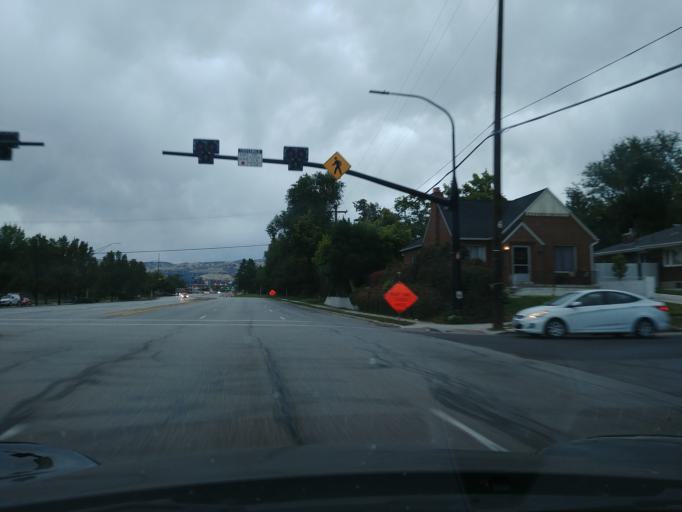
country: US
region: Utah
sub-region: Salt Lake County
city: Willard
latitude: 40.7154
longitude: -111.8534
